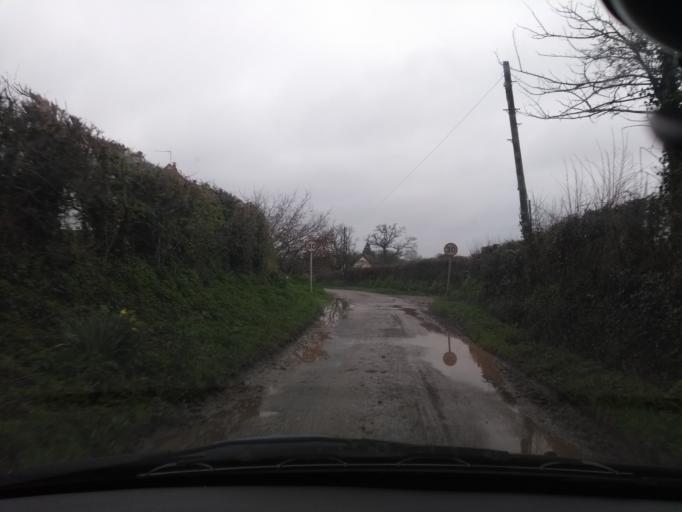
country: GB
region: England
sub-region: Somerset
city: Taunton
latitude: 51.0352
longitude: -3.1257
